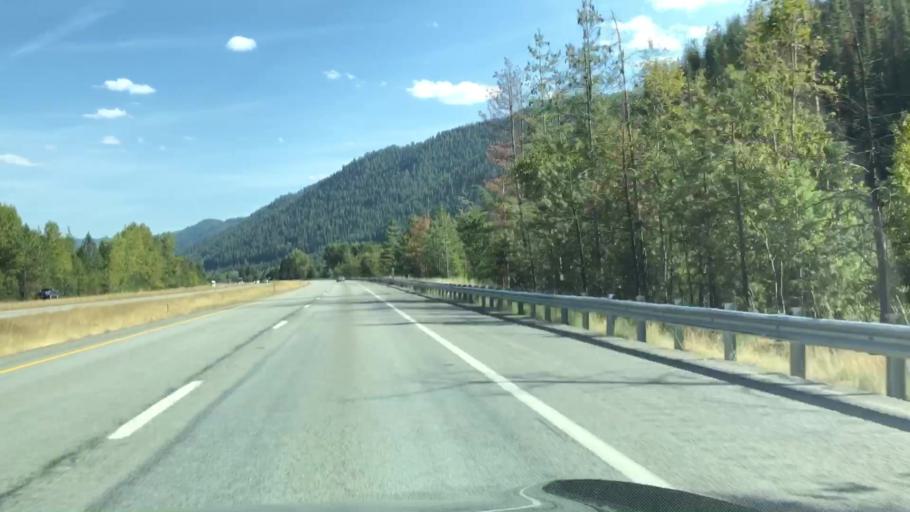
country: US
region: Idaho
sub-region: Shoshone County
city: Osburn
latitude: 47.5195
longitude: -116.0383
